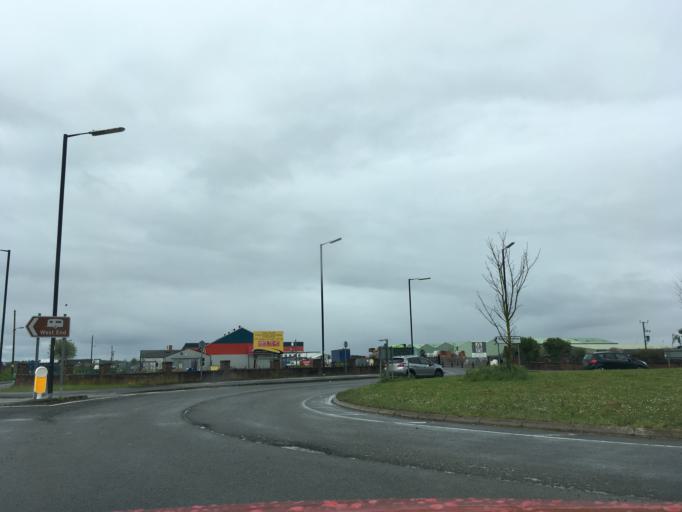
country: GB
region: England
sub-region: North Somerset
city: Hutton
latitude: 51.3391
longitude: -2.9279
